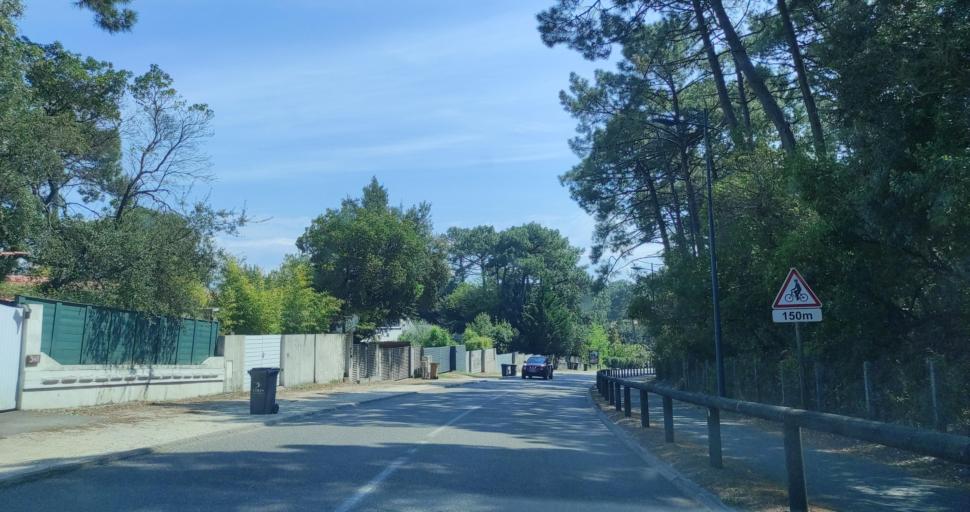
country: FR
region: Aquitaine
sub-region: Departement de la Gironde
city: Arcachon
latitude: 44.6878
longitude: -1.2385
